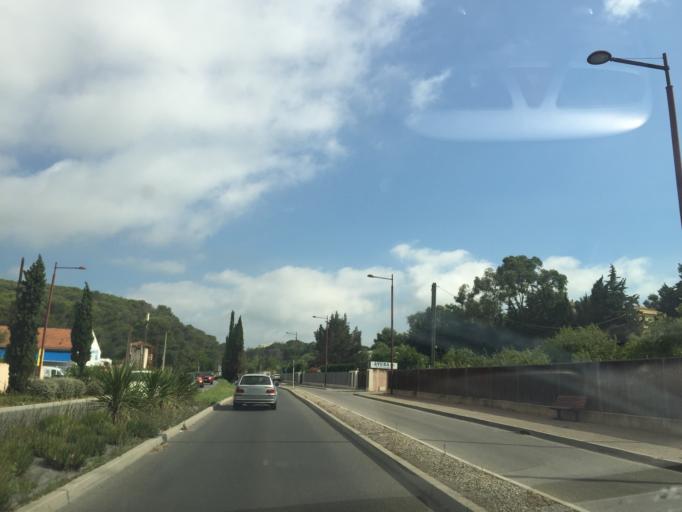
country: FR
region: Provence-Alpes-Cote d'Azur
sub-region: Departement des Alpes-Maritimes
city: Vallauris
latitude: 43.5829
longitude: 7.0899
